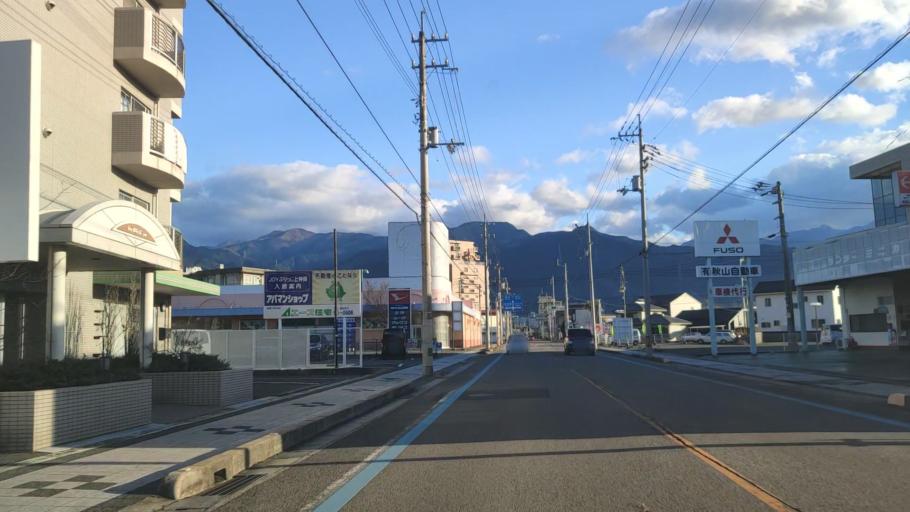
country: JP
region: Ehime
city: Saijo
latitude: 33.9126
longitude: 133.1795
